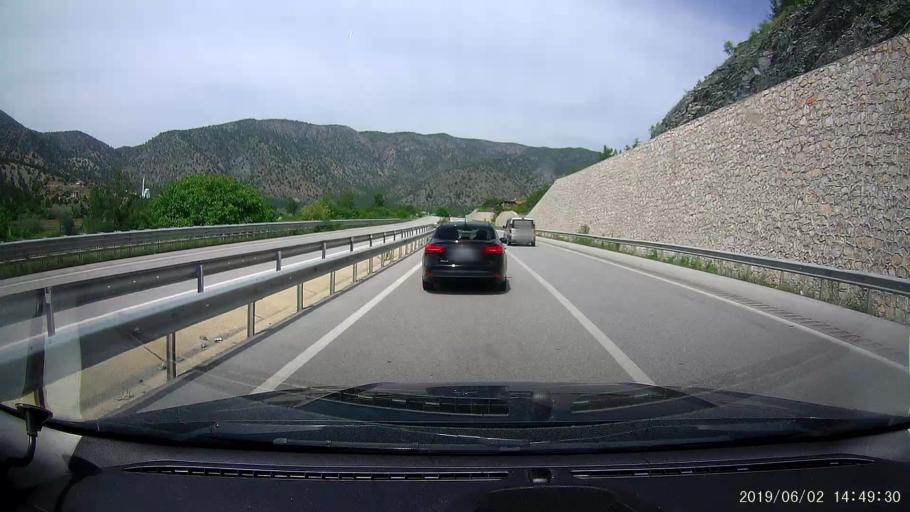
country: TR
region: Corum
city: Hacihamza
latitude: 41.0663
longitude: 34.5029
